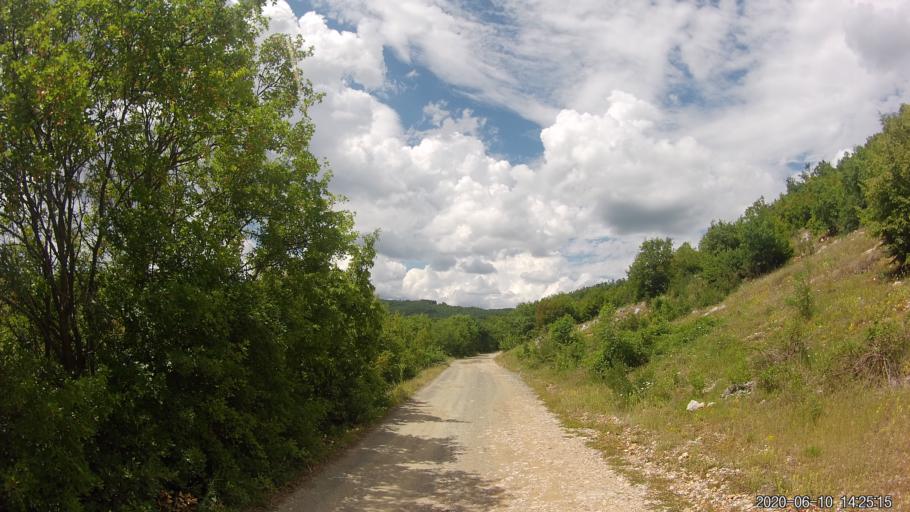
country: XK
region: Prizren
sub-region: Komuna e Therandes
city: Budakovo
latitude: 42.4061
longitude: 20.9166
